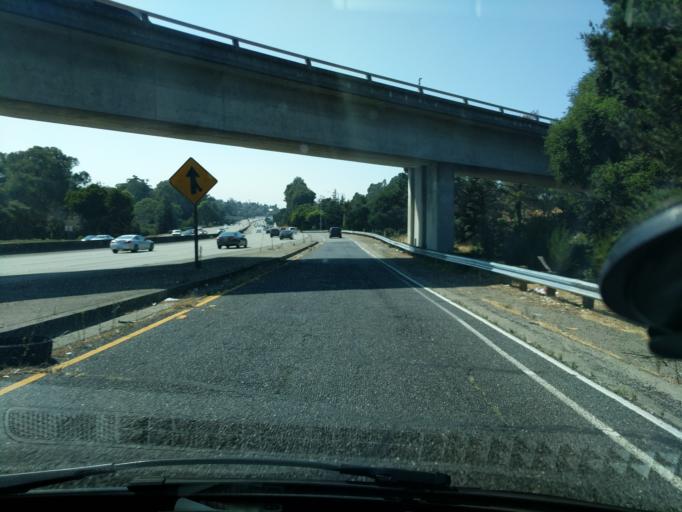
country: US
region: California
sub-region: Alameda County
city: San Leandro
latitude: 37.7839
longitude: -122.1782
